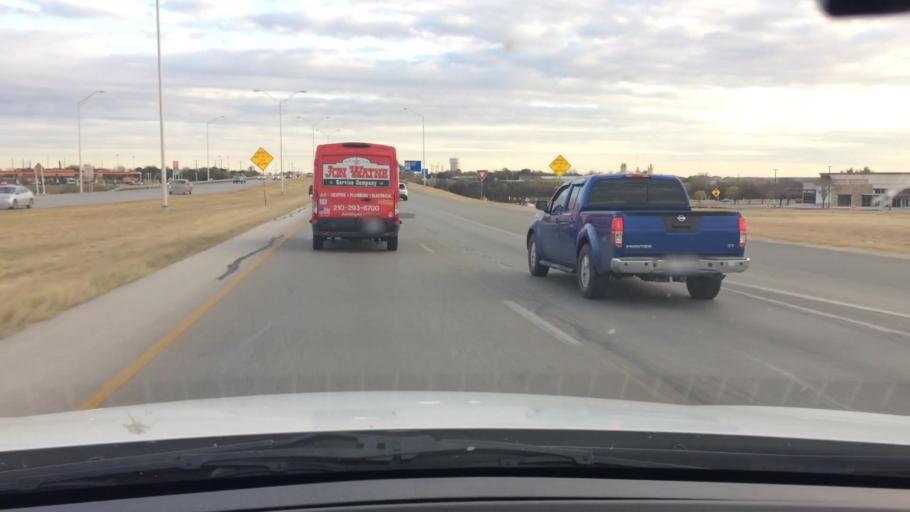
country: US
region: Texas
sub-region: Bexar County
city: Universal City
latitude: 29.5362
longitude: -98.3045
